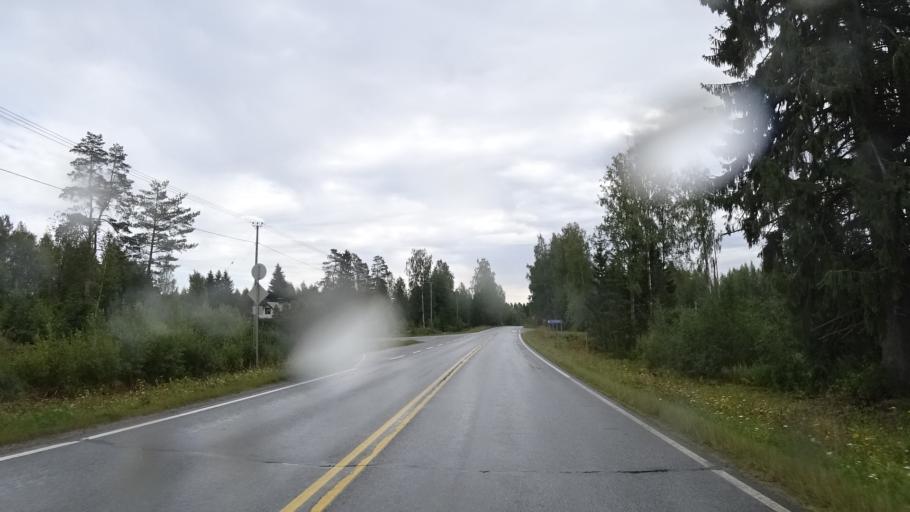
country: FI
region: North Karelia
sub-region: Keski-Karjala
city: Kesaelahti
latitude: 62.1051
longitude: 29.8302
